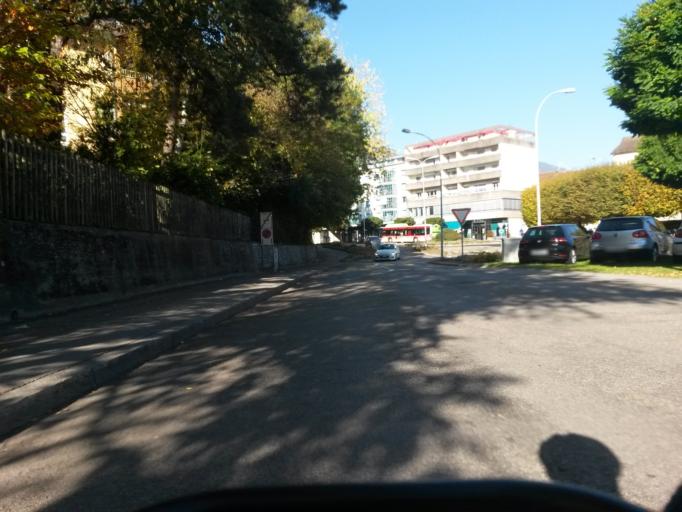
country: CH
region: Solothurn
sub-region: Bezirk Lebern
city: Grenchen
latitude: 47.1890
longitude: 7.3965
